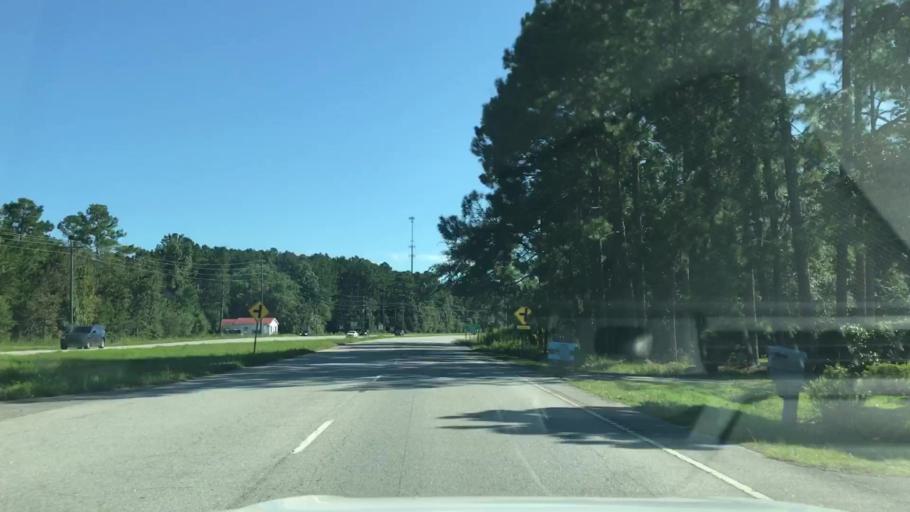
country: US
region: South Carolina
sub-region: Charleston County
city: Awendaw
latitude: 32.9922
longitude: -79.6458
